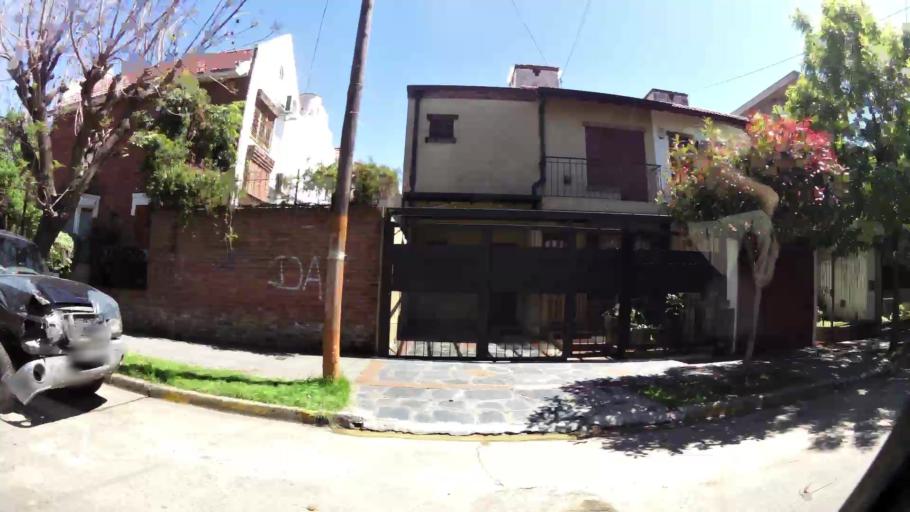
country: AR
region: Buenos Aires
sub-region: Partido de Quilmes
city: Quilmes
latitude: -34.7222
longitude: -58.2491
